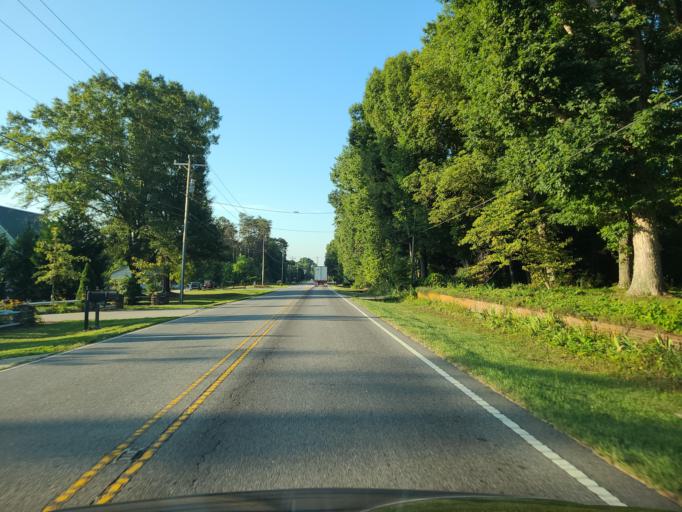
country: US
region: North Carolina
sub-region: Catawba County
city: Mountain View
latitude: 35.6659
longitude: -81.3823
